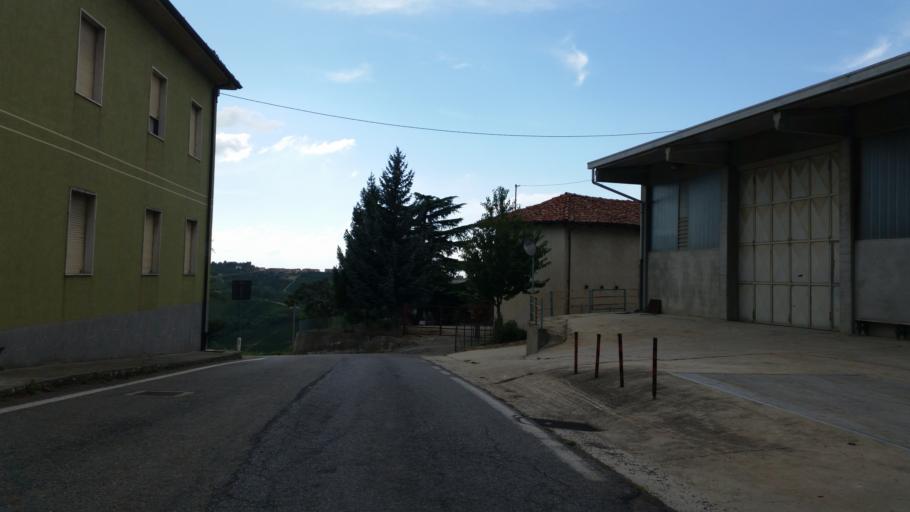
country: IT
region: Piedmont
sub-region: Provincia di Cuneo
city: Neviglie
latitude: 44.6909
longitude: 8.1151
